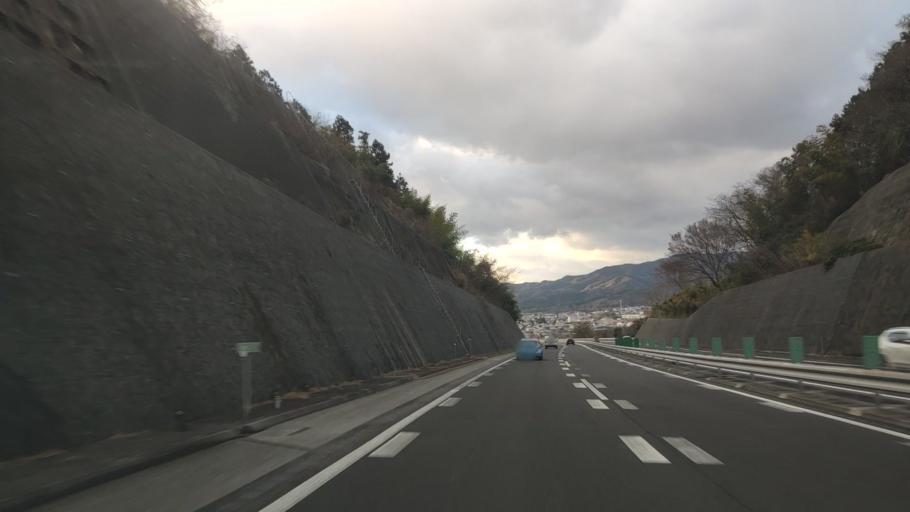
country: JP
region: Ehime
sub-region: Shikoku-chuo Shi
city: Matsuyama
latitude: 33.7918
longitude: 132.9140
